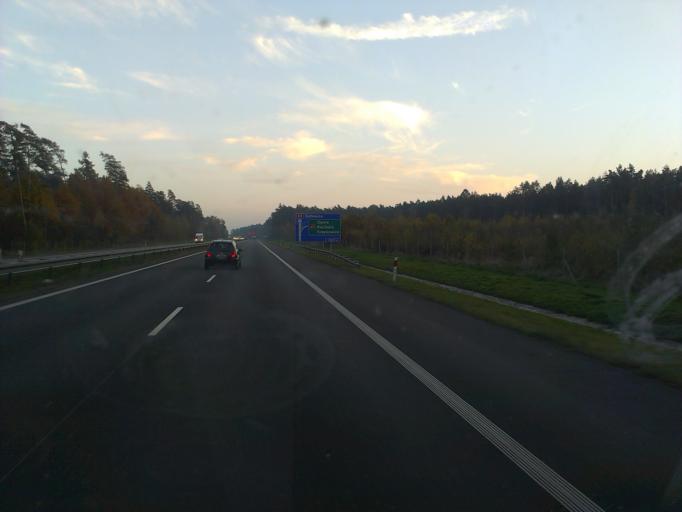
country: PL
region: Opole Voivodeship
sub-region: Powiat opolski
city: Proszkow
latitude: 50.5446
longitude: 17.8966
